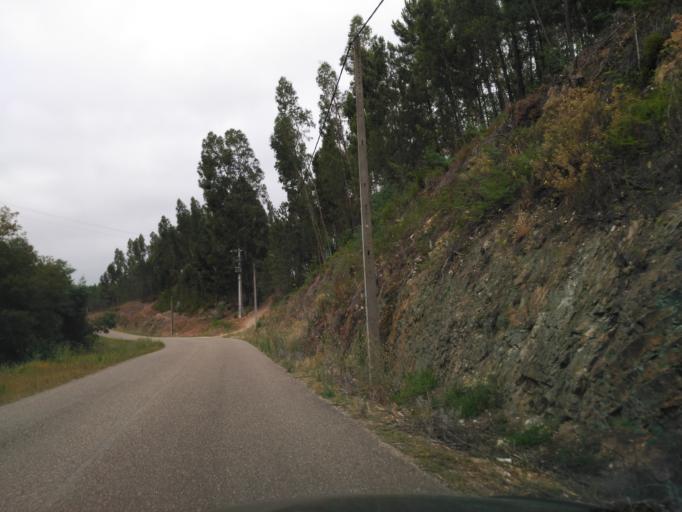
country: PT
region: Santarem
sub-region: Abrantes
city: Alferrarede
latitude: 39.5554
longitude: -8.1466
